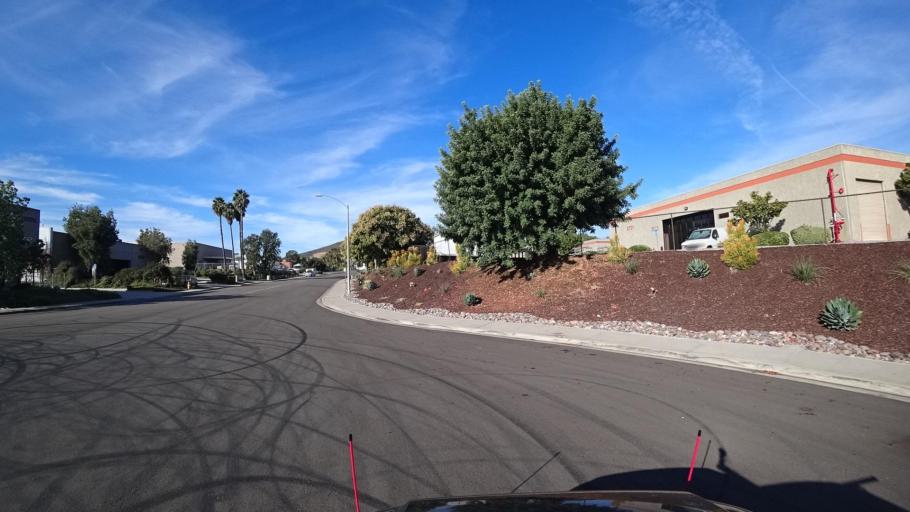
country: US
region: California
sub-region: San Diego County
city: Casa de Oro-Mount Helix
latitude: 32.7296
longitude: -116.9669
